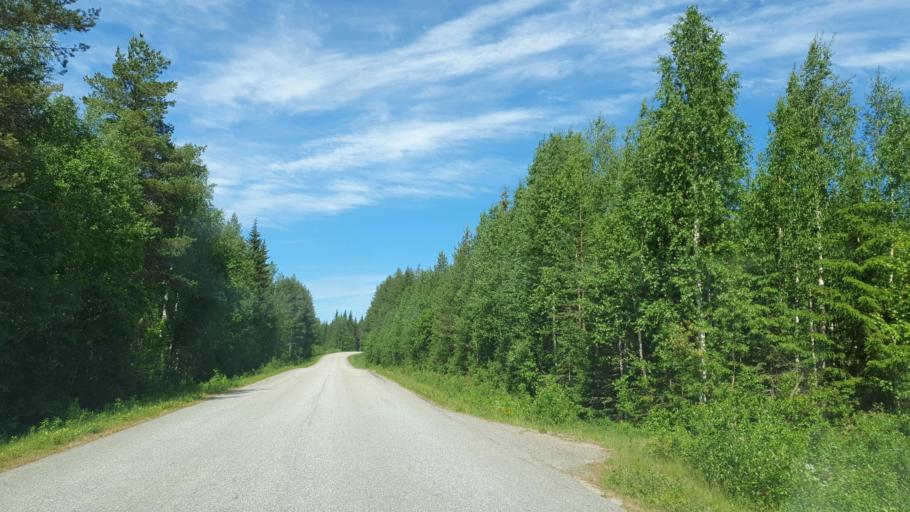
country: FI
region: Kainuu
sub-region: Kehys-Kainuu
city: Suomussalmi
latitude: 64.5907
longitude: 29.1056
